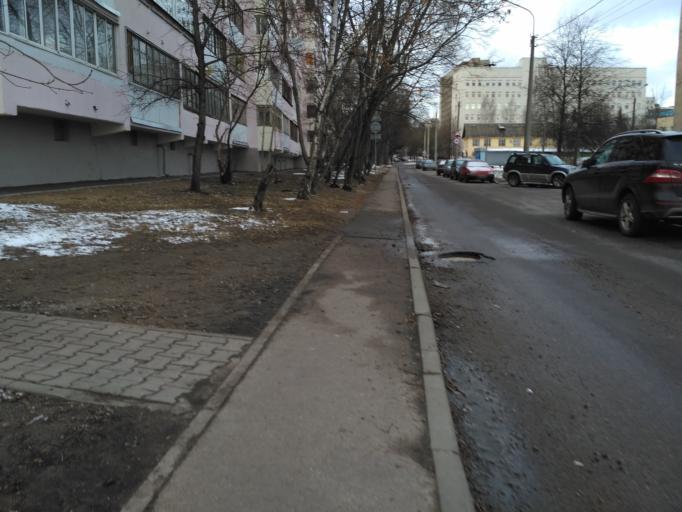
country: BY
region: Minsk
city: Minsk
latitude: 53.9244
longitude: 27.5844
